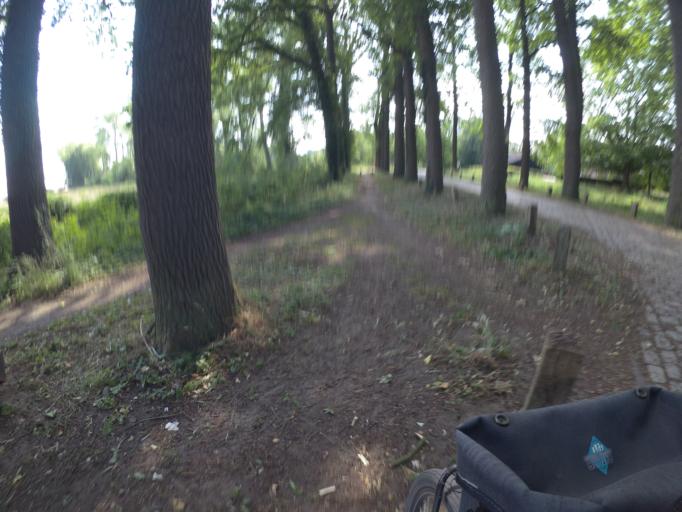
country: NL
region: North Brabant
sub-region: Gemeente Haaren
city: Haaren
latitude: 51.5902
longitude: 5.2323
